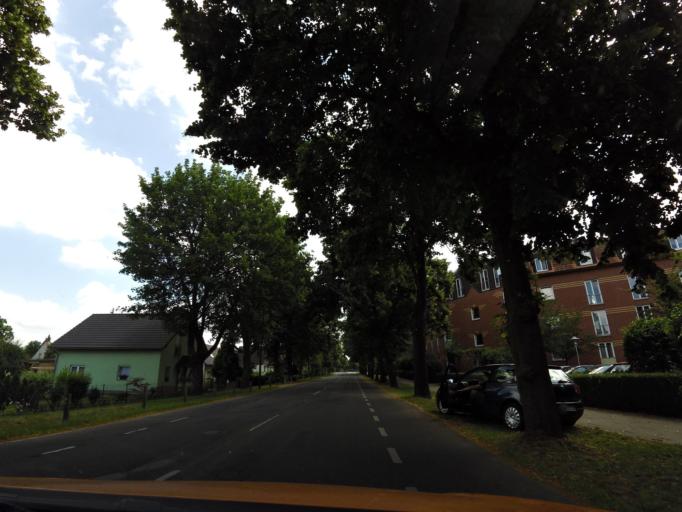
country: DE
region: Brandenburg
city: Nauen
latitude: 52.6093
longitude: 12.8602
